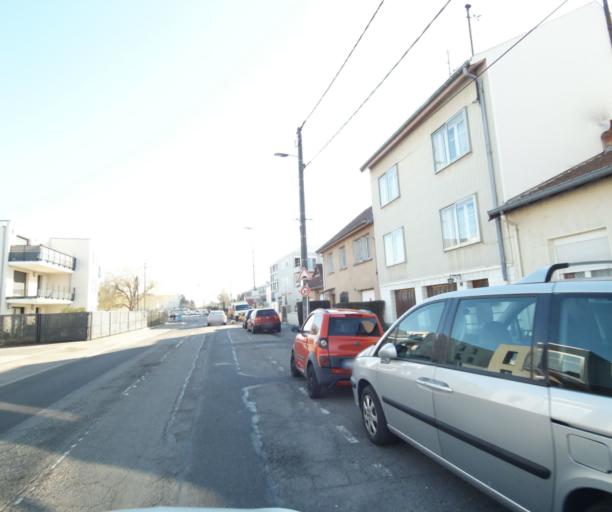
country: FR
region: Lorraine
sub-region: Departement de Meurthe-et-Moselle
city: Saint-Max
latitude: 48.6986
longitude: 6.2148
